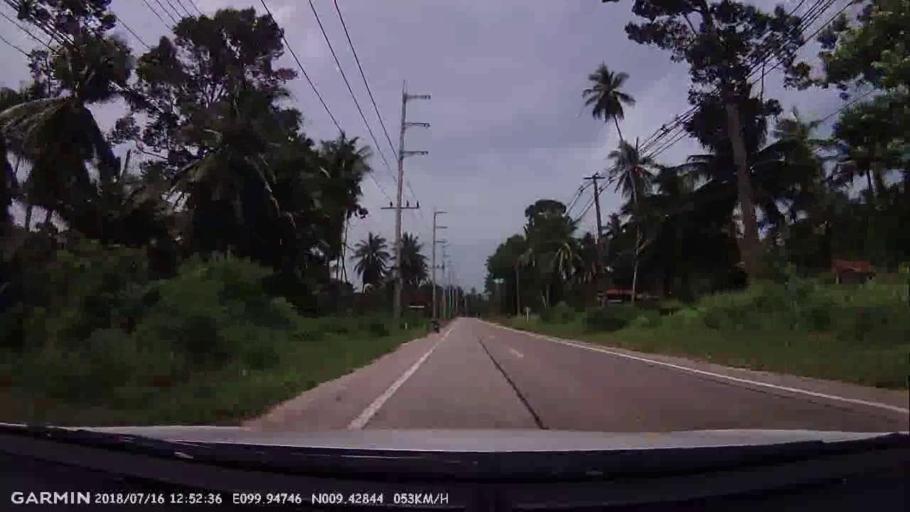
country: TH
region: Surat Thani
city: Ko Samui
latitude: 9.4283
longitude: 99.9476
